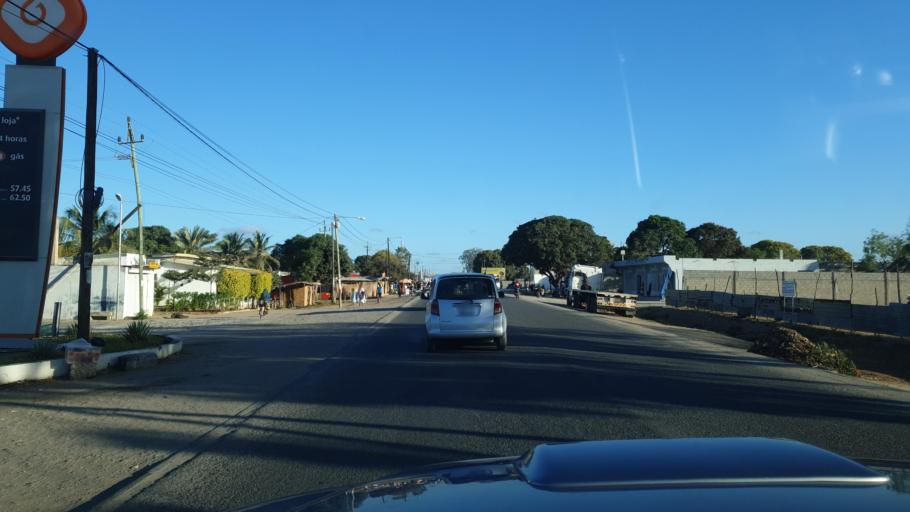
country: MZ
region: Nampula
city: Nacala
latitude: -14.5772
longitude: 40.6816
